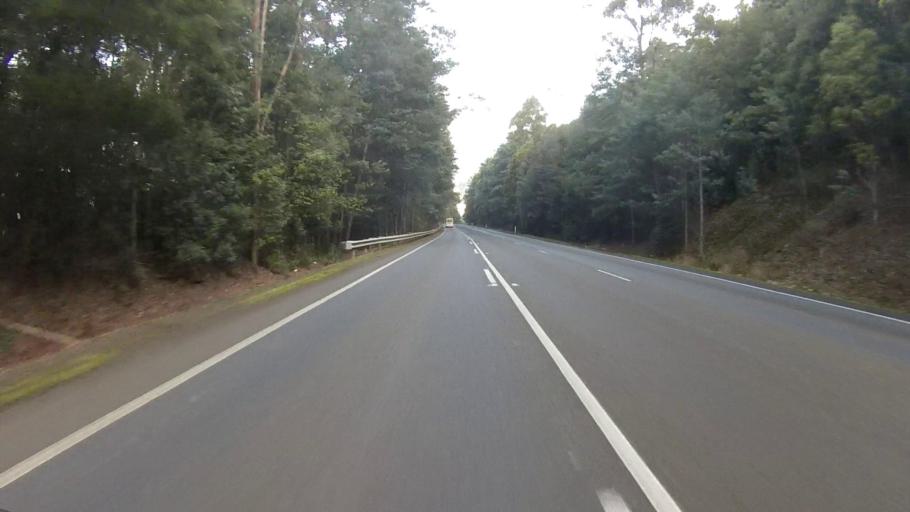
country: AU
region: Tasmania
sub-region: Sorell
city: Sorell
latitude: -43.0045
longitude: 147.9267
